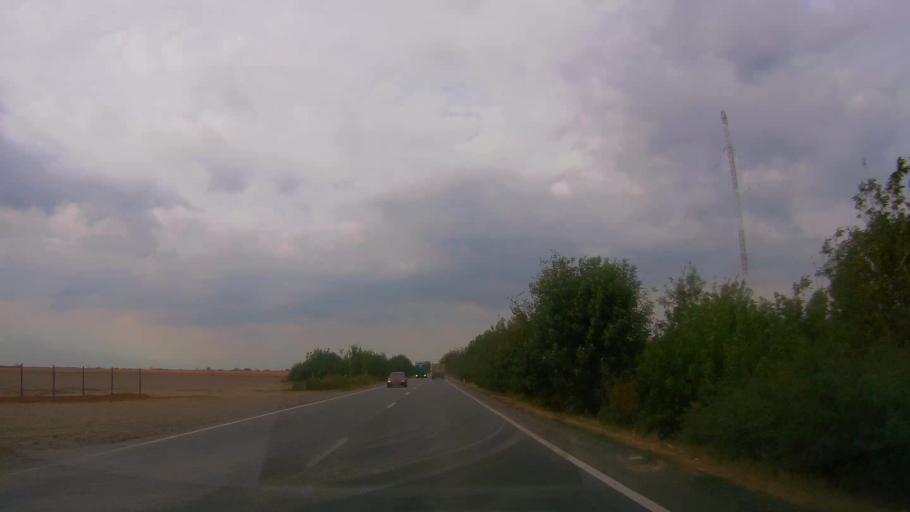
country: RO
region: Satu Mare
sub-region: Comuna Botiz
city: Botiz
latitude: 47.8549
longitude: 22.9784
